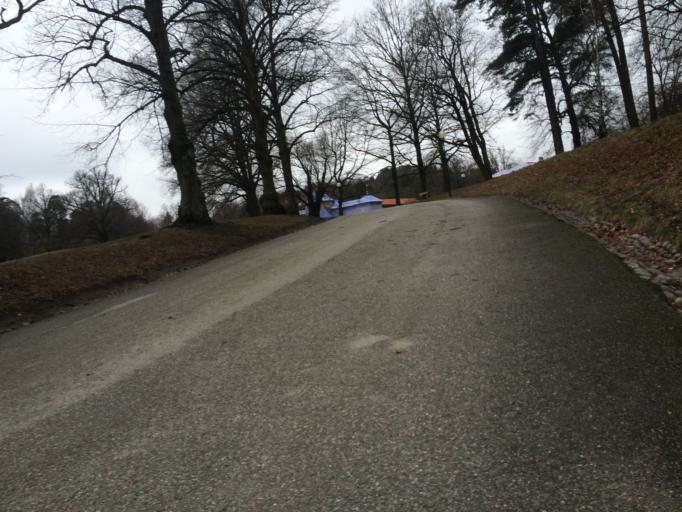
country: SE
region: Stockholm
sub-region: Norrtalje Kommun
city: Bergshamra
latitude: 59.3641
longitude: 18.0330
